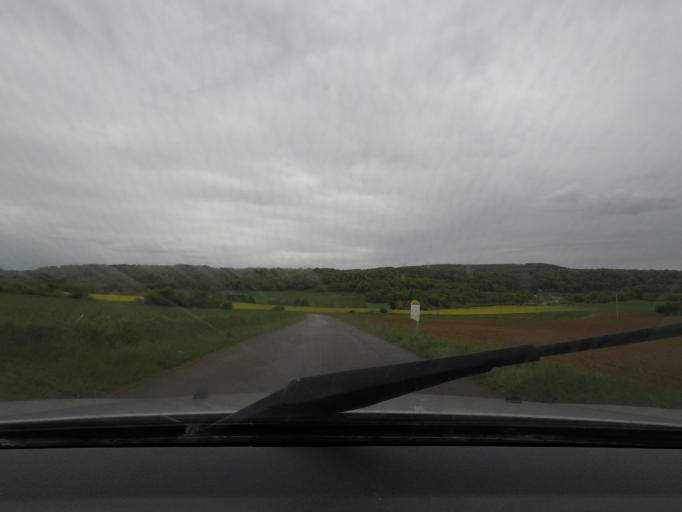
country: BE
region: Wallonia
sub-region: Province du Luxembourg
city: Rouvroy
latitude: 49.5020
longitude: 5.4406
